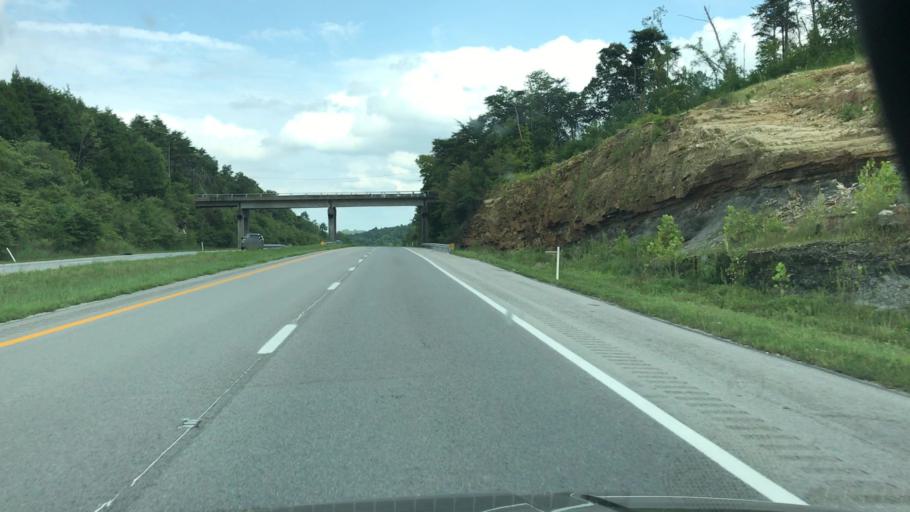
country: US
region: Kentucky
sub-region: Hopkins County
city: Dawson Springs
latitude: 37.1547
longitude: -87.7799
